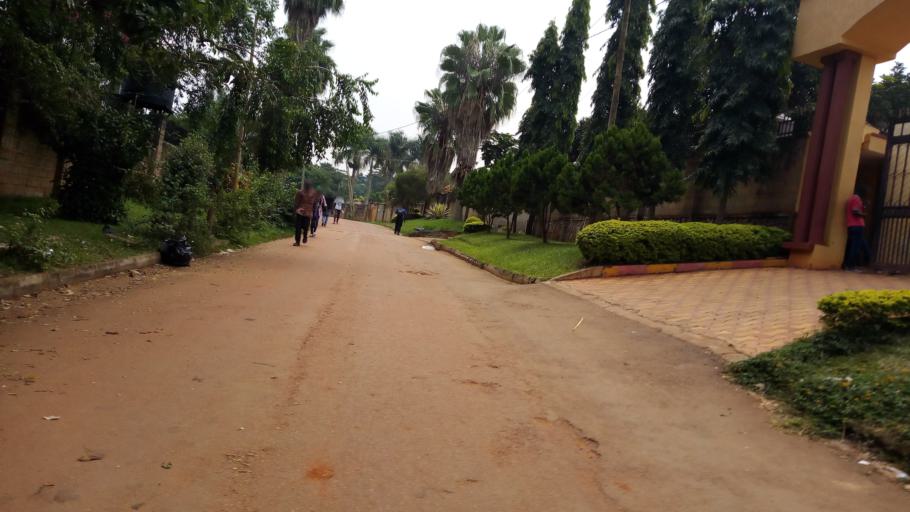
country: UG
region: Central Region
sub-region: Wakiso District
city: Kireka
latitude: 0.3213
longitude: 32.6300
